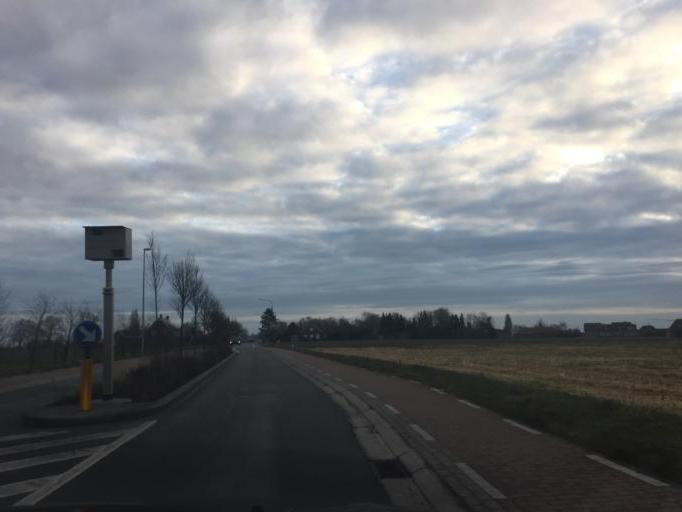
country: BE
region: Flanders
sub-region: Provincie West-Vlaanderen
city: Hooglede
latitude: 50.9831
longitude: 3.0952
